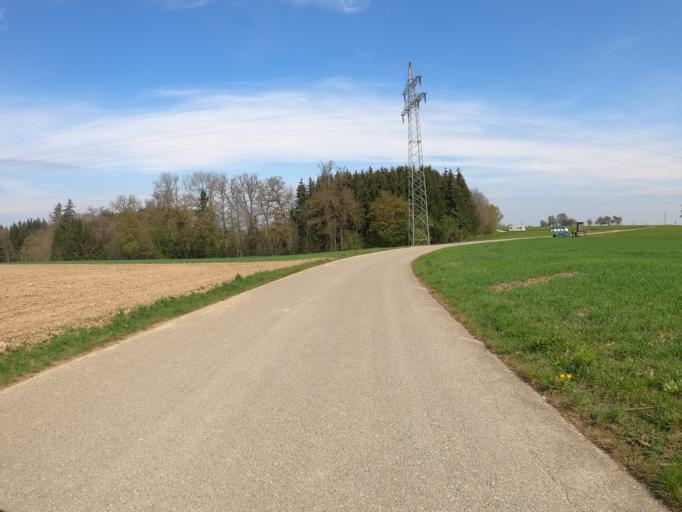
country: DE
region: Bavaria
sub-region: Swabia
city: Rieden an der Kotz
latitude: 48.3734
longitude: 10.2175
